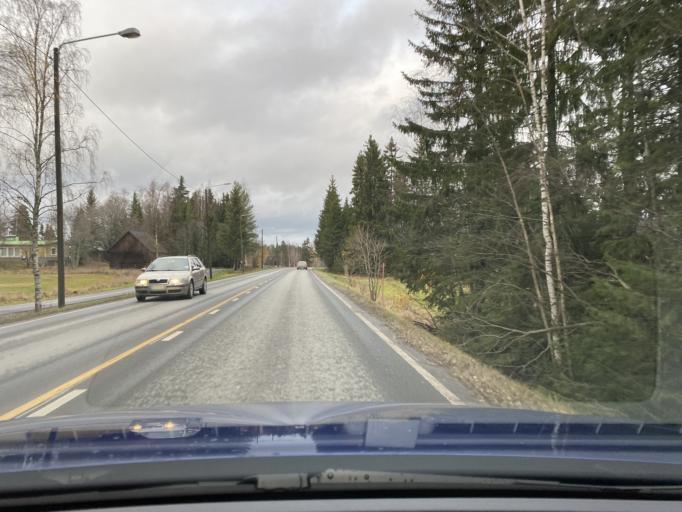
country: FI
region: Pirkanmaa
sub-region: Tampere
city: Lempaeaelae
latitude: 61.3422
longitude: 23.7548
